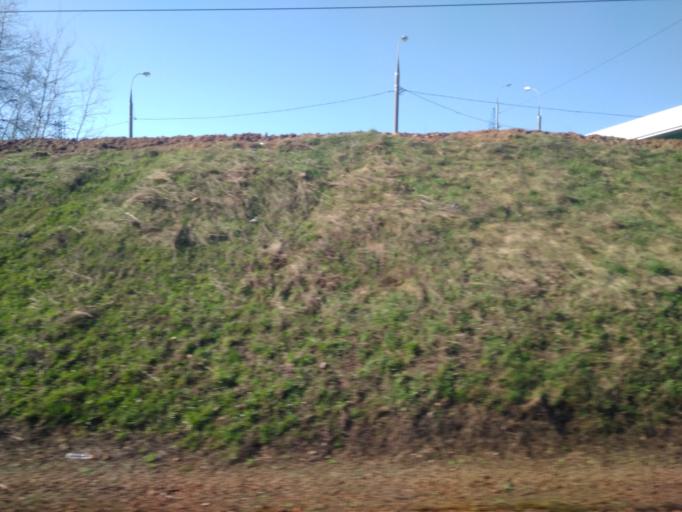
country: RU
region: Moscow
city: Strogino
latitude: 55.8333
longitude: 37.3881
